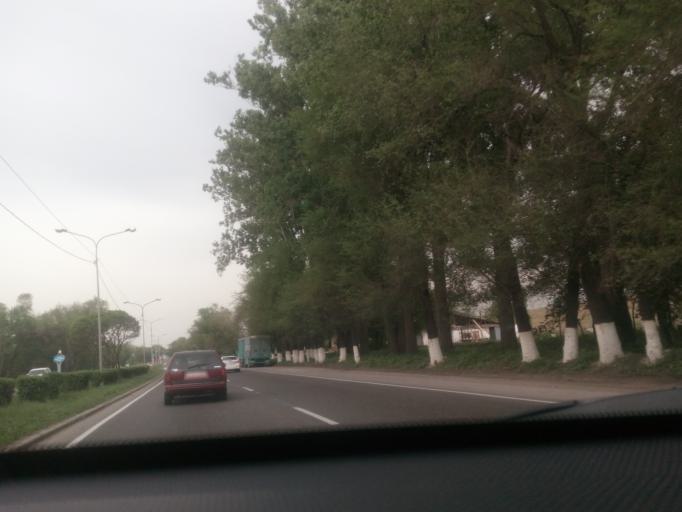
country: KZ
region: Almaty Oblysy
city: Burunday
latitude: 43.2215
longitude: 76.7166
